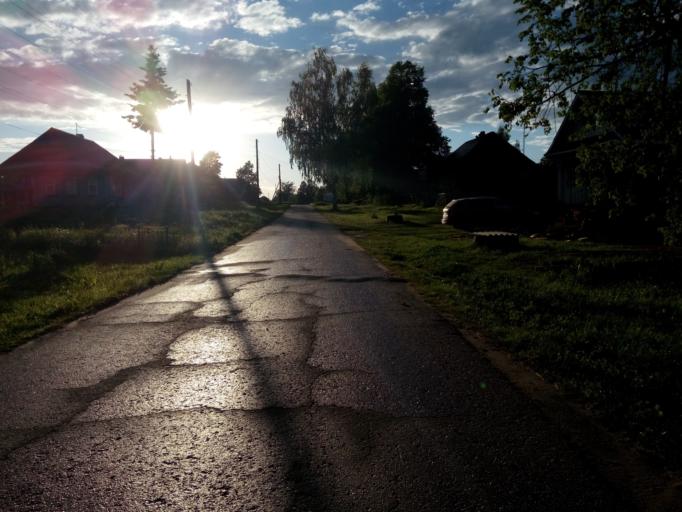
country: RU
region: Nizjnij Novgorod
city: Voskresenskoye
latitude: 56.7736
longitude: 45.5512
